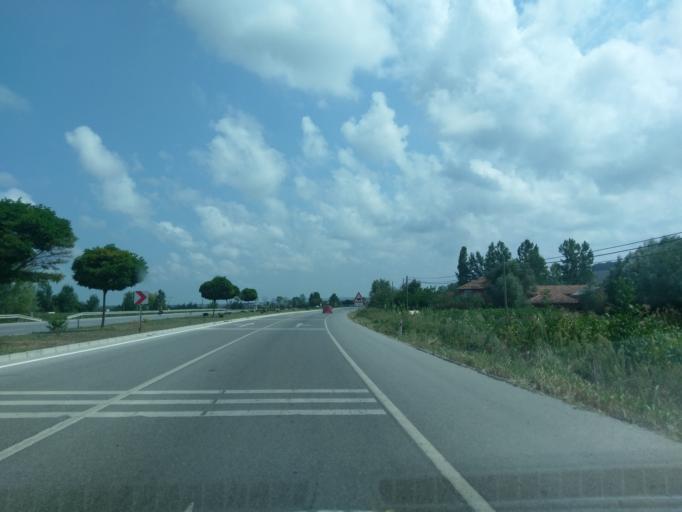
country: TR
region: Samsun
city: Alacam
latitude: 41.6123
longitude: 35.7098
